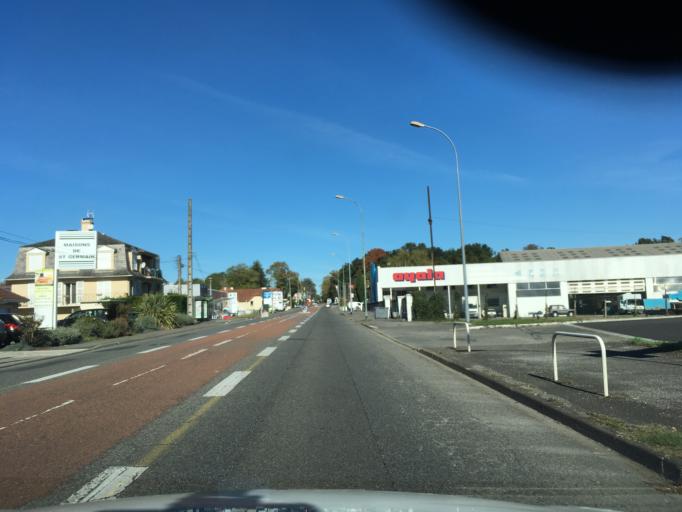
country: FR
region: Aquitaine
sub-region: Departement des Pyrenees-Atlantiques
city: Lons
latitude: 43.3319
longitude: -0.3796
